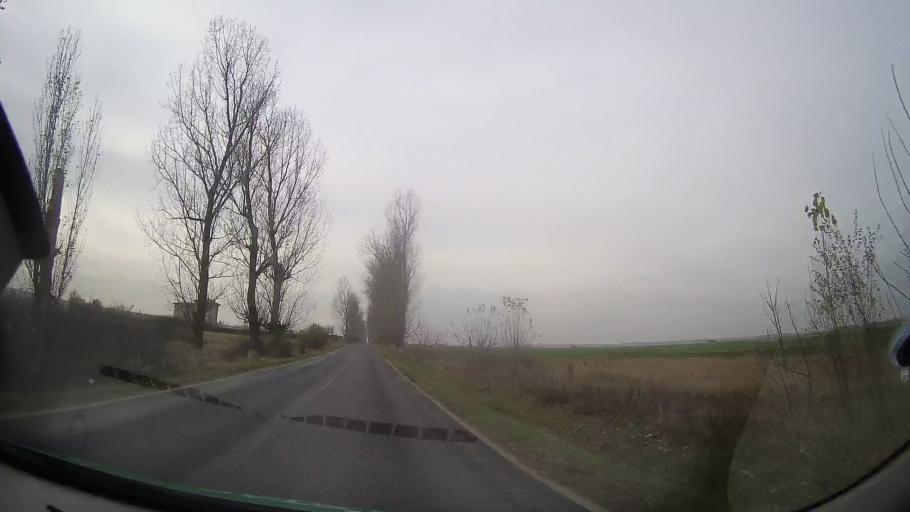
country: RO
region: Prahova
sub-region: Comuna Balta Doamnei
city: Balta Doamnei
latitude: 44.7443
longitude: 26.1670
